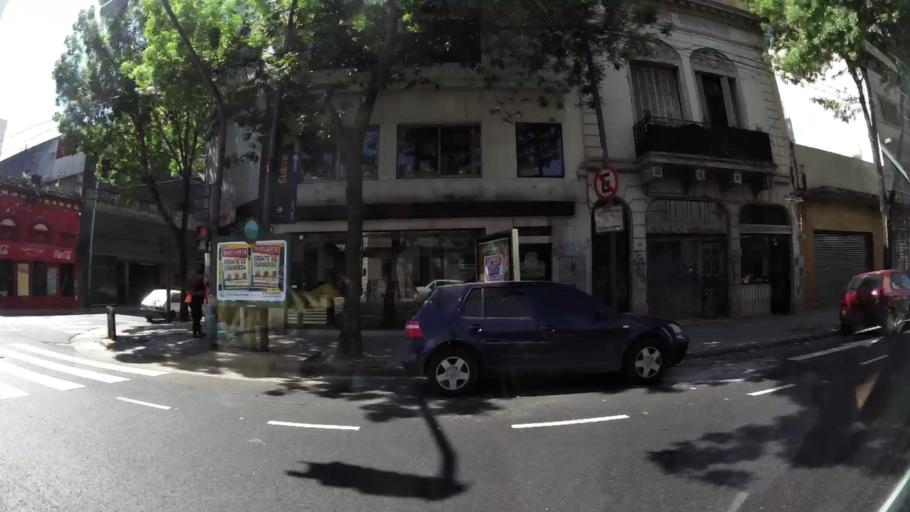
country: AR
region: Buenos Aires F.D.
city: Buenos Aires
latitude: -34.6222
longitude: -58.3827
